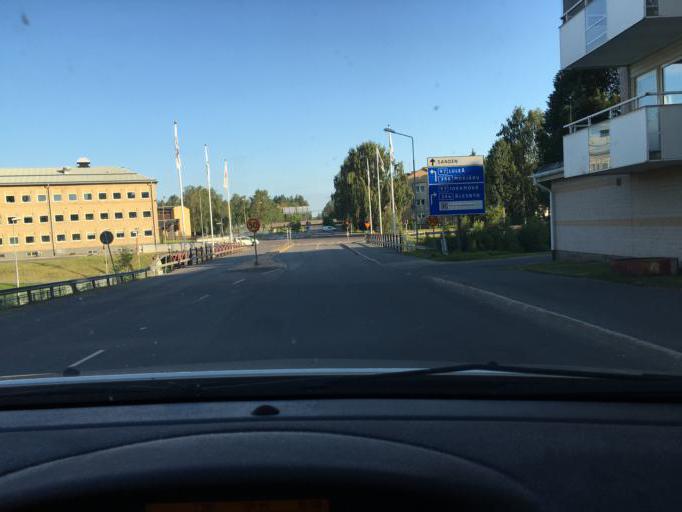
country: SE
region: Norrbotten
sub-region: Bodens Kommun
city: Boden
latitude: 65.8236
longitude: 21.6895
